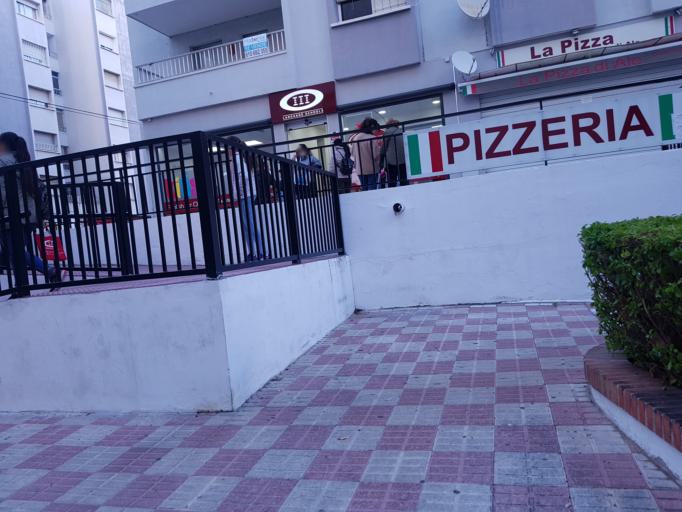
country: ES
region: Andalusia
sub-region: Provincia de Malaga
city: Marbella
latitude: 36.5166
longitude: -4.8872
